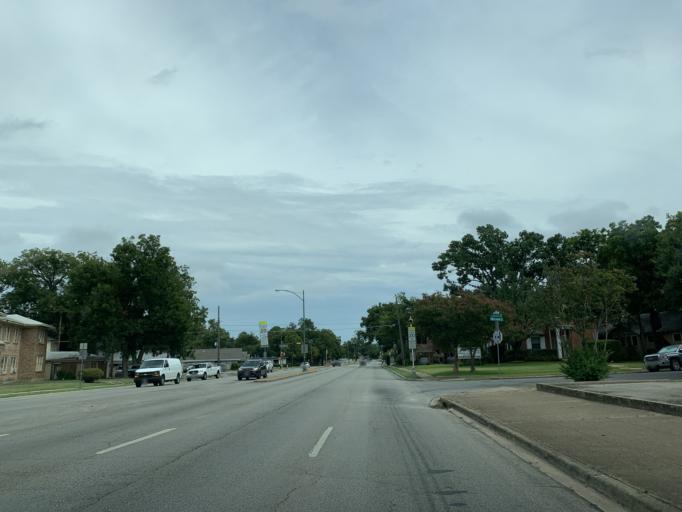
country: US
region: Texas
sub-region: Dallas County
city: Cockrell Hill
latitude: 32.7447
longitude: -96.8456
